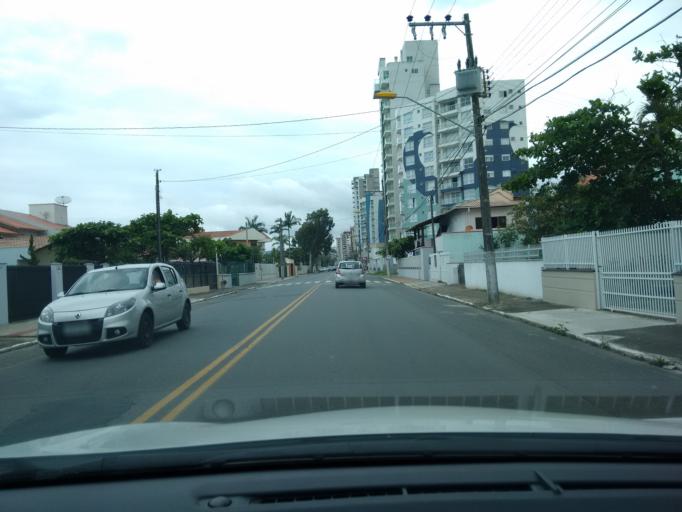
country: BR
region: Santa Catarina
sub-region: Penha
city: Penha
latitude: -26.7514
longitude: -48.6776
